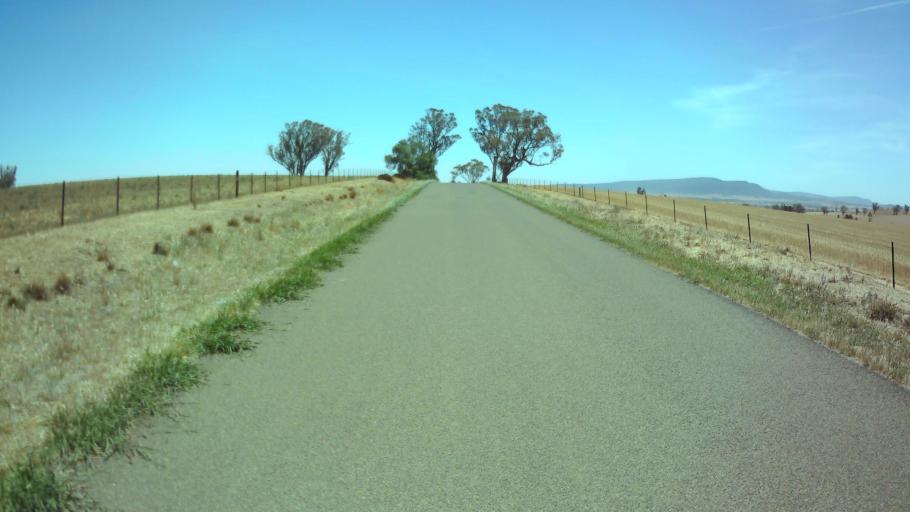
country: AU
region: New South Wales
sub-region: Weddin
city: Grenfell
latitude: -34.0544
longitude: 148.2274
